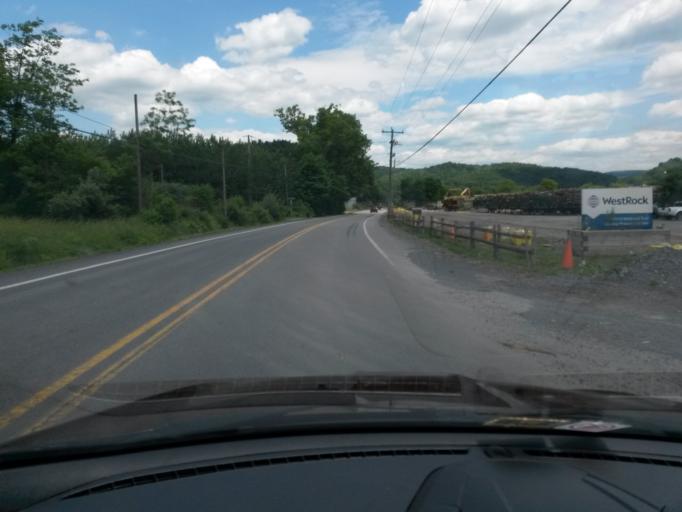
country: US
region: West Virginia
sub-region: Greenbrier County
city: Rainelle
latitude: 37.9534
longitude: -80.6627
